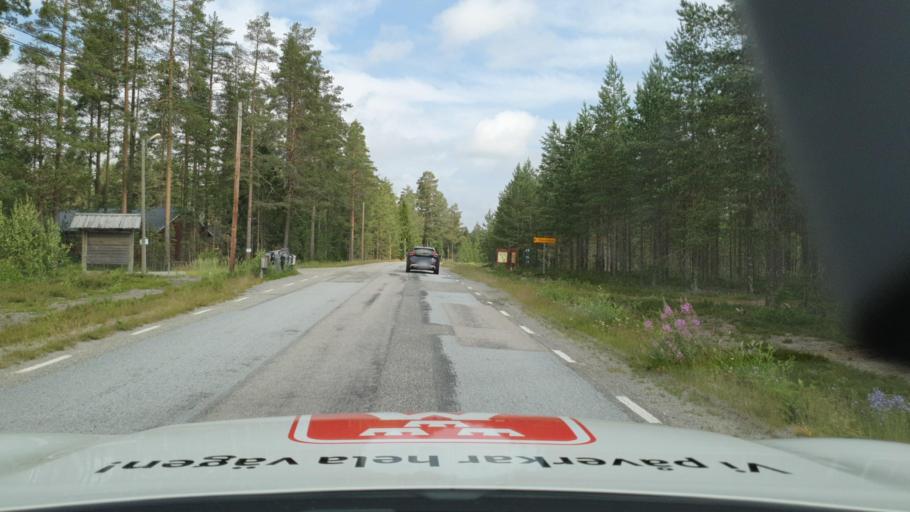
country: SE
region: Vaesterbotten
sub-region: Umea Kommun
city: Roback
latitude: 63.9193
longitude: 20.1447
